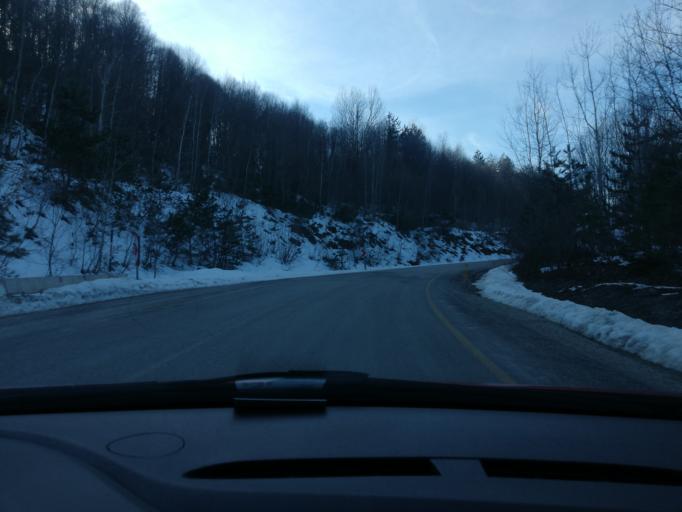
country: TR
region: Kastamonu
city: Cide
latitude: 41.8543
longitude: 33.0696
